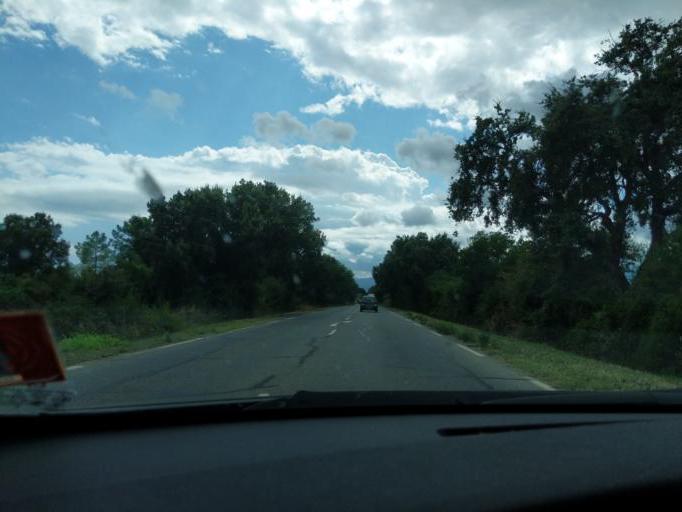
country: FR
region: Corsica
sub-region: Departement de la Haute-Corse
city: Ghisonaccia
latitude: 42.0487
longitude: 9.4278
